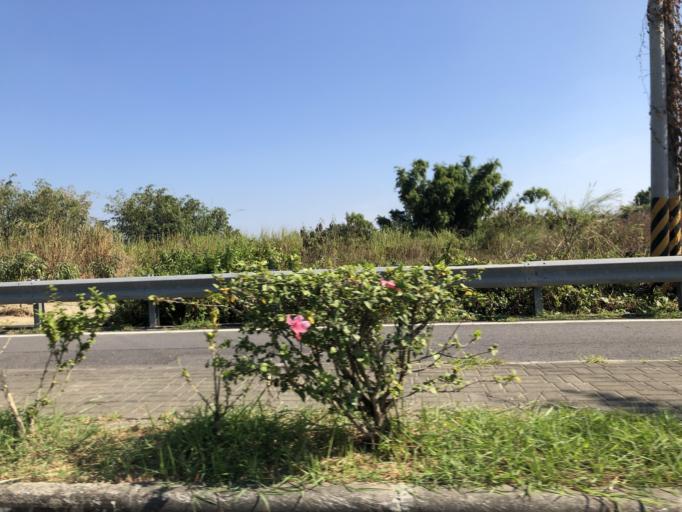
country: TW
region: Taiwan
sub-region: Tainan
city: Tainan
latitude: 23.0316
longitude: 120.3225
